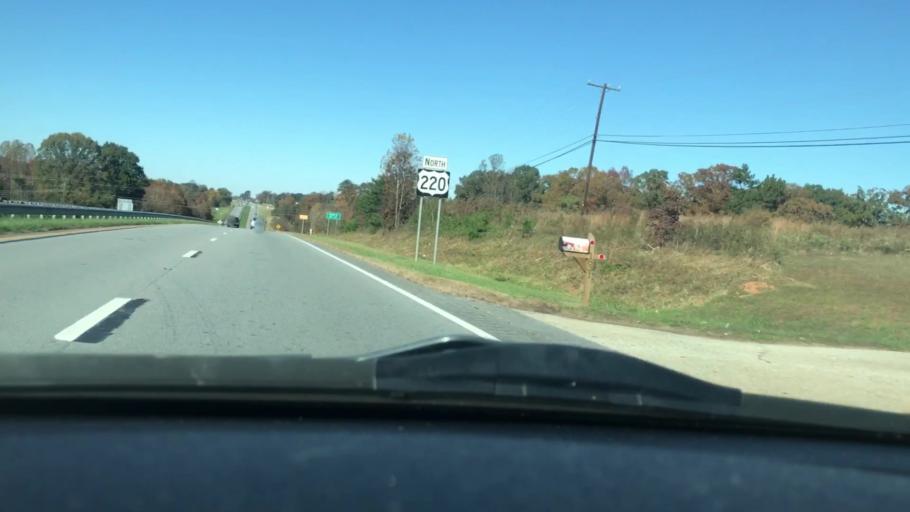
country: US
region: North Carolina
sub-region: Guilford County
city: Stokesdale
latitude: 36.2982
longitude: -79.9404
